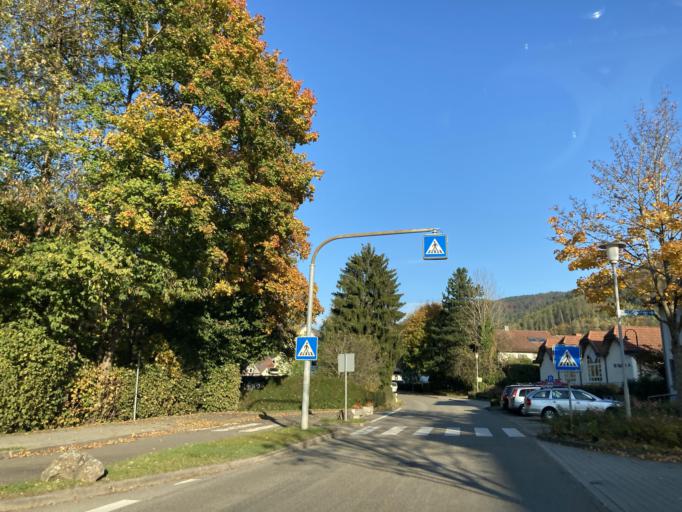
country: DE
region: Baden-Wuerttemberg
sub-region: Freiburg Region
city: Buchenbach
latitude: 47.9613
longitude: 8.0111
